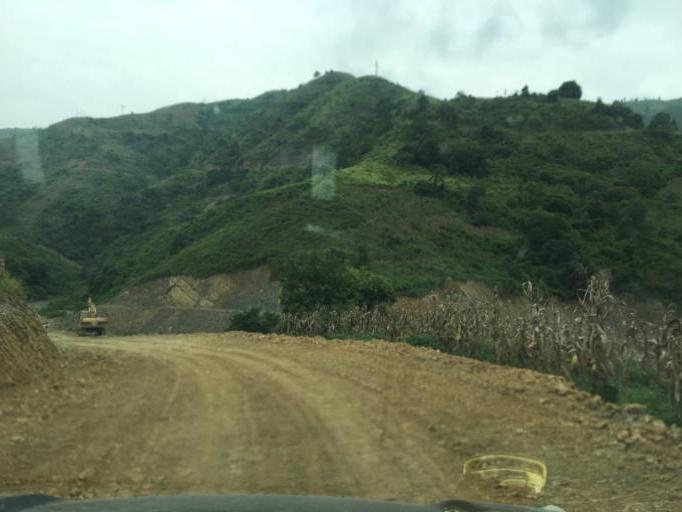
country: CN
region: Guangxi Zhuangzu Zizhiqu
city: Tongle
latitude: 25.1235
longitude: 106.4177
